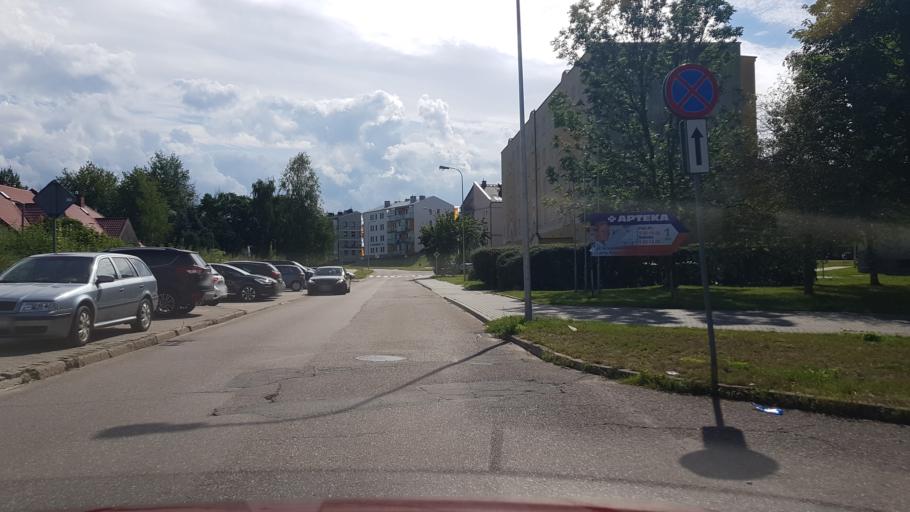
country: PL
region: West Pomeranian Voivodeship
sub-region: Koszalin
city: Koszalin
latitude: 54.2117
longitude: 16.1907
